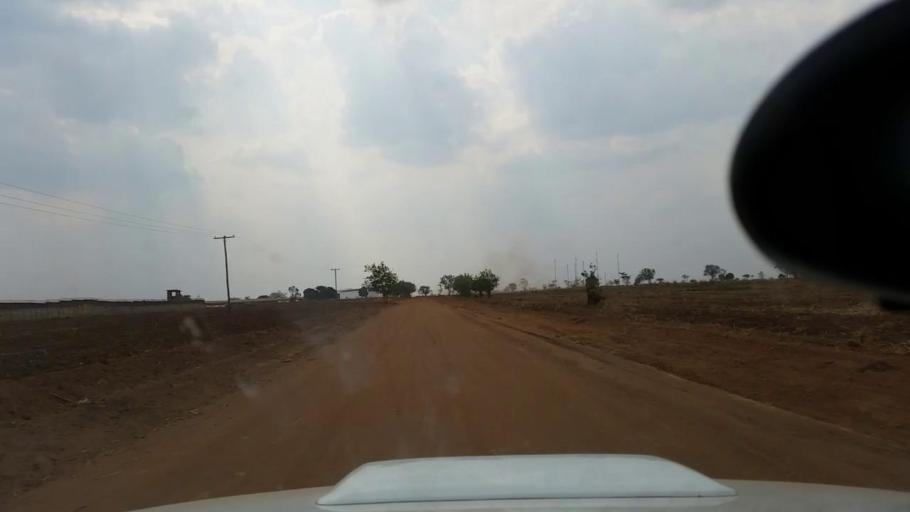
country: MW
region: Central Region
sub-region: Lilongwe District
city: Lilongwe
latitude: -13.7954
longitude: 33.7730
